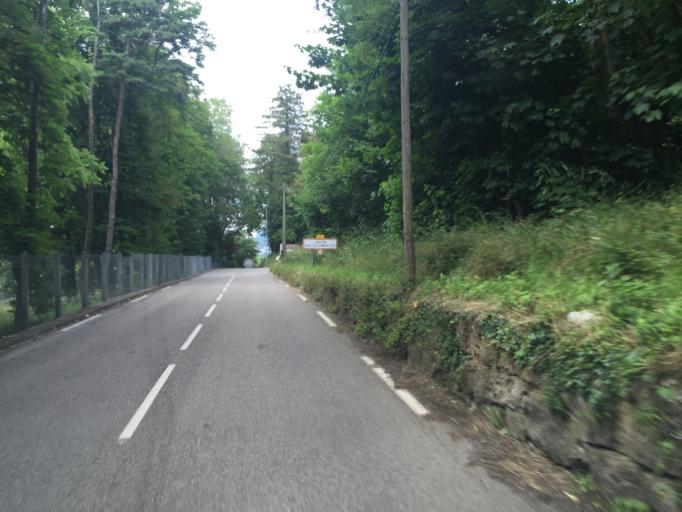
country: FR
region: Rhone-Alpes
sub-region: Departement de la Savoie
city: Jacob-Bellecombette
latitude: 45.5463
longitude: 5.9206
